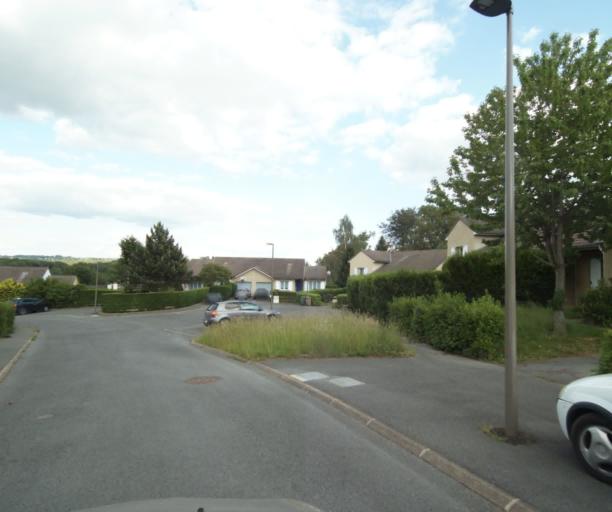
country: FR
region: Champagne-Ardenne
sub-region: Departement des Ardennes
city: Montcy-Notre-Dame
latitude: 49.7902
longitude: 4.7253
